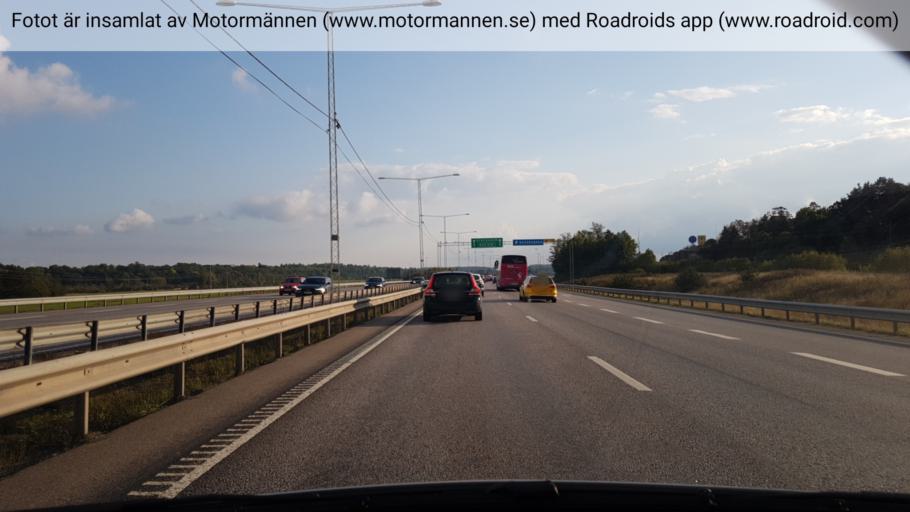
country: SE
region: Stockholm
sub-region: Sigtuna Kommun
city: Rosersberg
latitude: 59.5799
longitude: 17.9006
